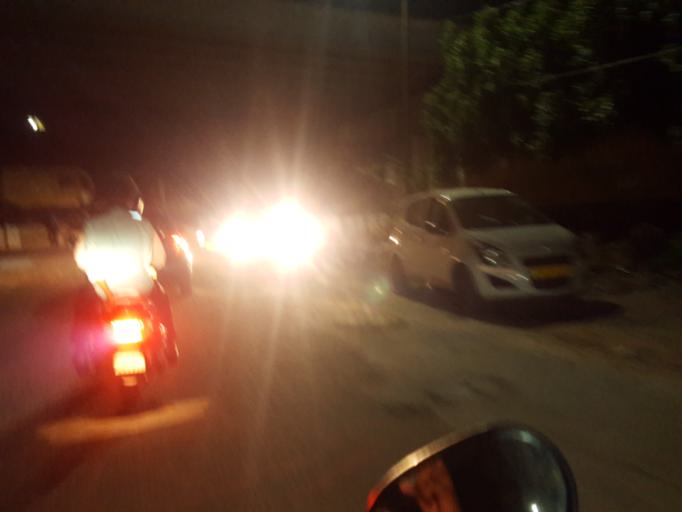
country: IN
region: Telangana
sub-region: Rangareddi
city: Kukatpalli
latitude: 17.4890
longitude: 78.3924
